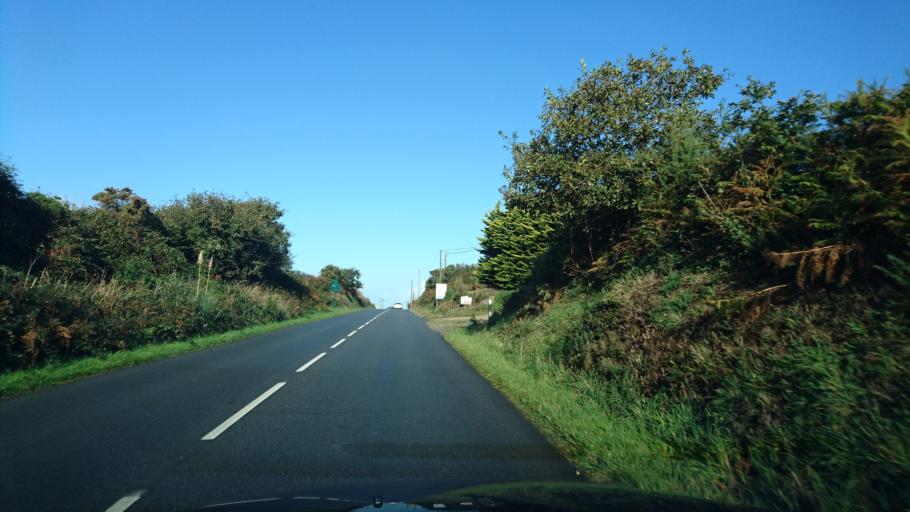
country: FR
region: Brittany
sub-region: Departement du Finistere
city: Lampaul-Plouarzel
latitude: 48.4433
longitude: -4.7501
